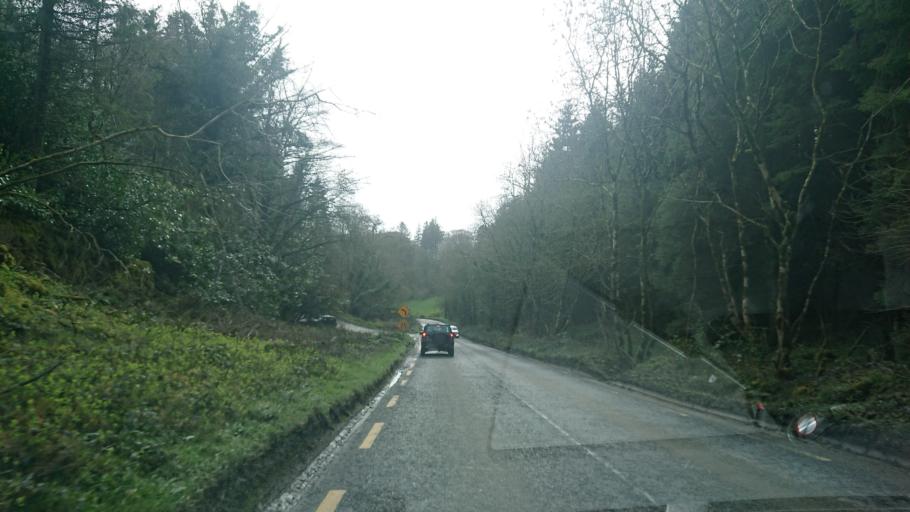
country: IE
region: Leinster
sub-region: Kildare
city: Eadestown
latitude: 53.1810
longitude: -6.5607
